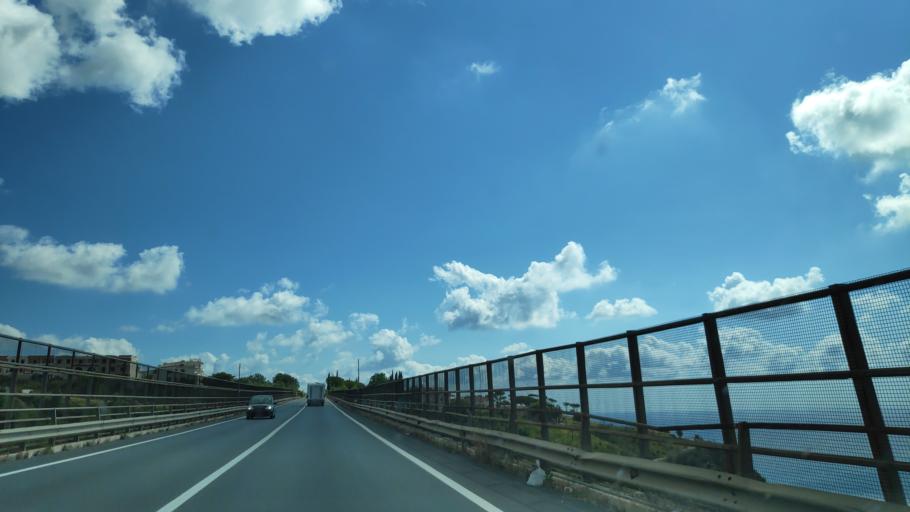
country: IT
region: Calabria
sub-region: Provincia di Cosenza
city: San Nicola Arcella
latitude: 39.8584
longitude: 15.7976
